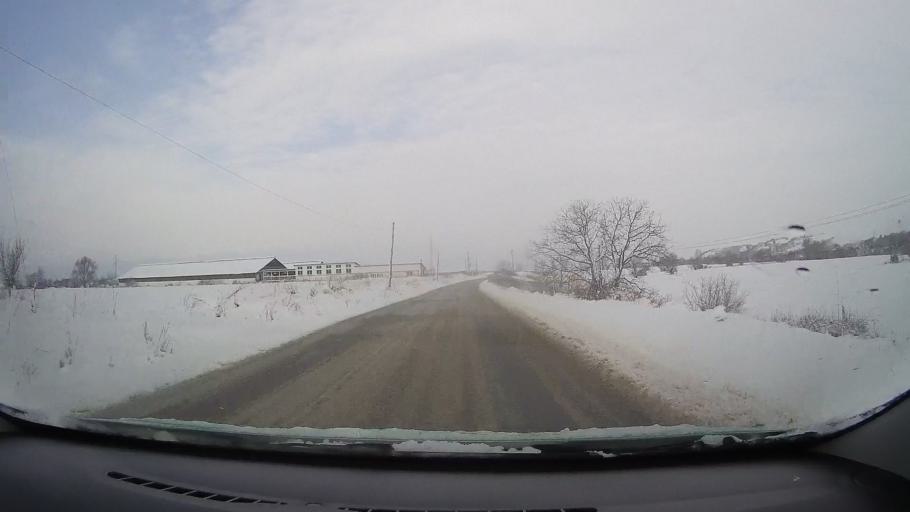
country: RO
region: Alba
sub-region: Comuna Pianu
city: Pianu de Jos
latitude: 45.9517
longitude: 23.4784
